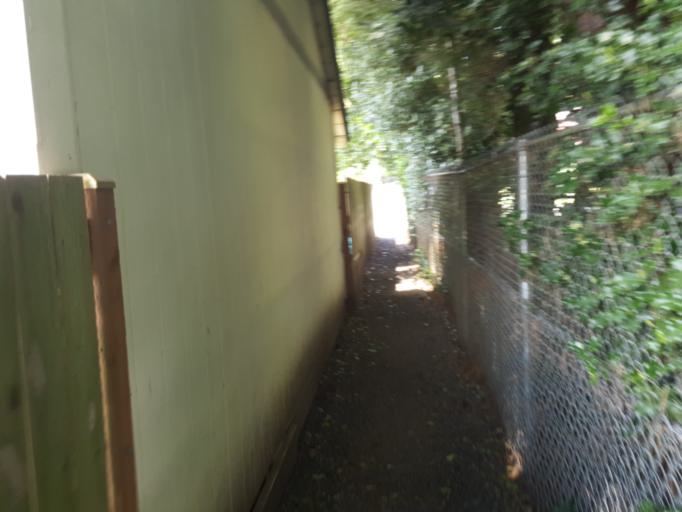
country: US
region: Washington
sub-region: Pierce County
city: University Place
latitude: 47.2059
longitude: -122.5564
